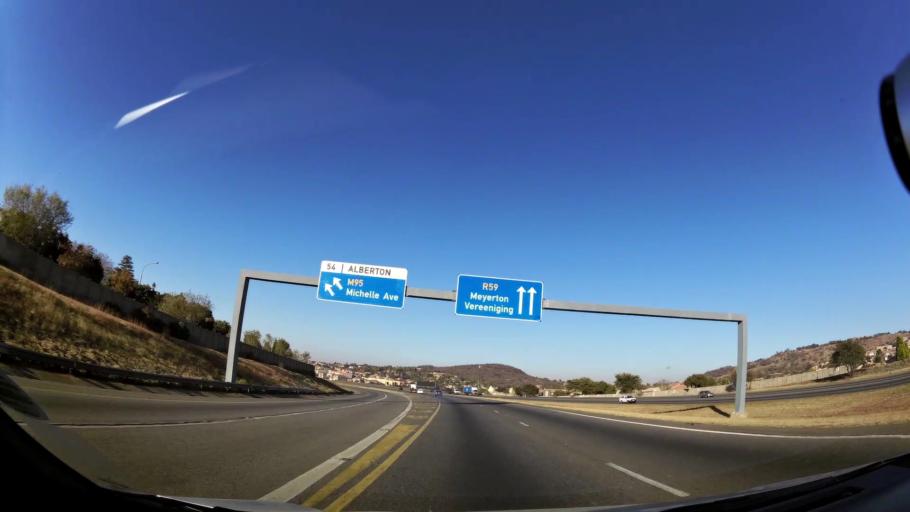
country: ZA
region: Gauteng
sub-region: Ekurhuleni Metropolitan Municipality
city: Germiston
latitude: -26.2820
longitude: 28.1022
